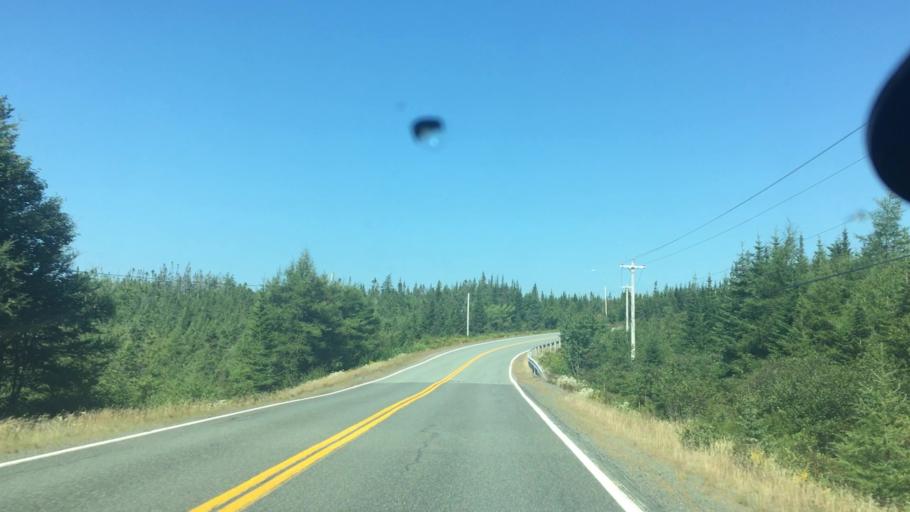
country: CA
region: Nova Scotia
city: Antigonish
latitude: 45.0070
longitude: -62.1050
